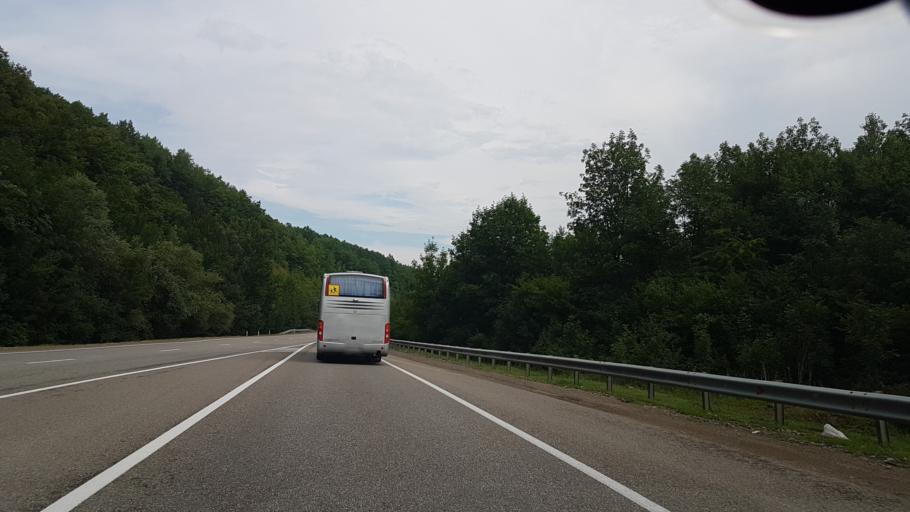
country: RU
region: Krasnodarskiy
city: Goryachiy Klyuch
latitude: 44.5752
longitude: 39.0013
